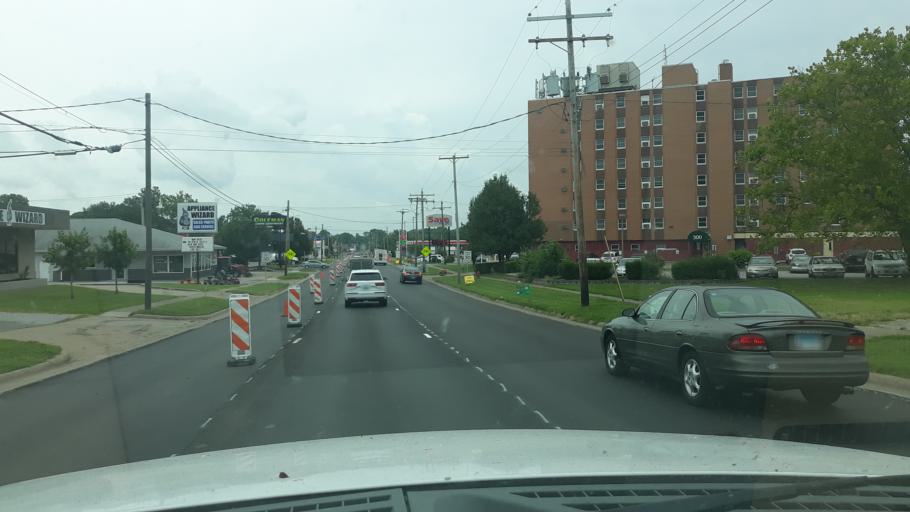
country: US
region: Illinois
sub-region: Jackson County
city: Carbondale
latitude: 37.7254
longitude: -89.2150
